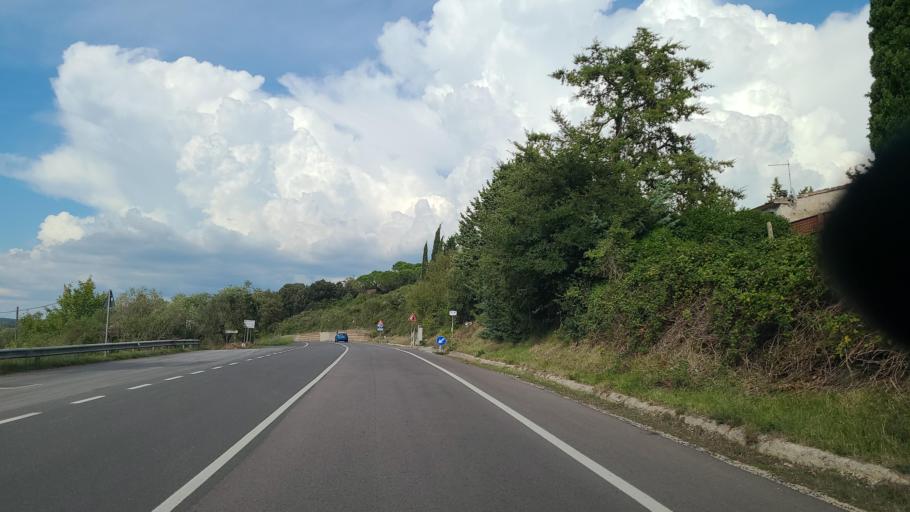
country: IT
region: Tuscany
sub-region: Province of Pisa
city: Volterra
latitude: 43.3909
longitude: 10.9527
